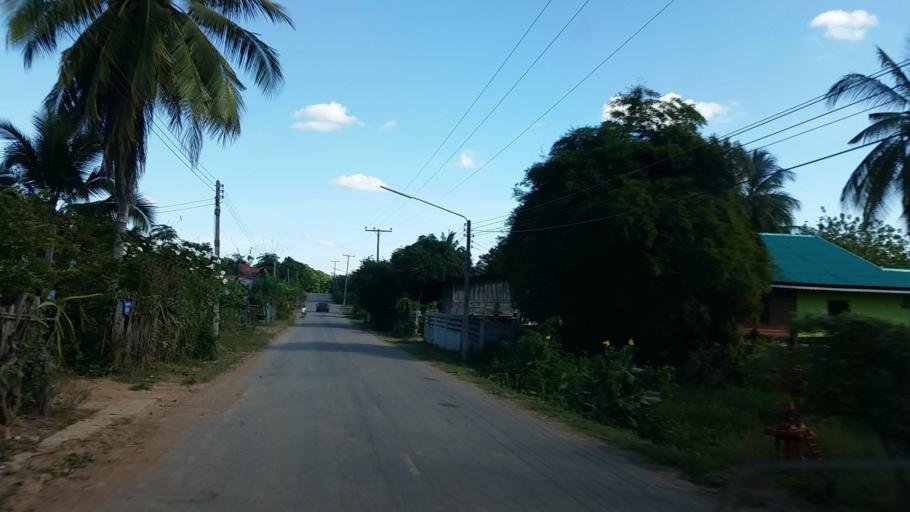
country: TH
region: Chaiyaphum
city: Thep Sathit
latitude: 15.5567
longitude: 101.4432
